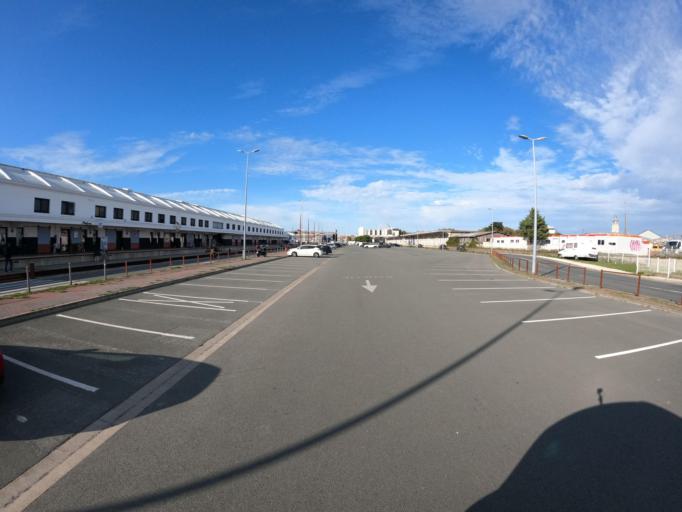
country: FR
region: Poitou-Charentes
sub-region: Departement de la Charente-Maritime
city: La Rochelle
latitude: 46.1502
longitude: -1.1499
